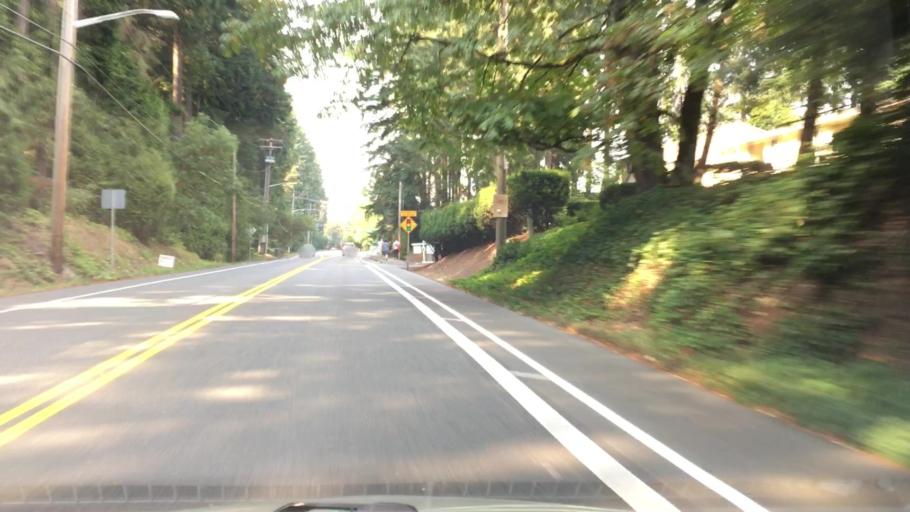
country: US
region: Washington
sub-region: King County
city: Inglewood-Finn Hill
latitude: 47.7262
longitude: -122.2436
